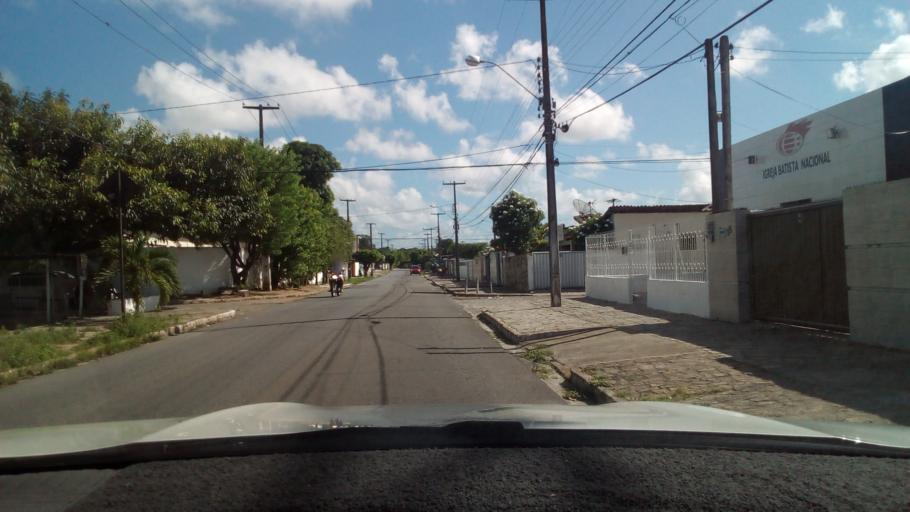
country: BR
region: Paraiba
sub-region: Joao Pessoa
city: Joao Pessoa
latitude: -7.1327
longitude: -34.8509
